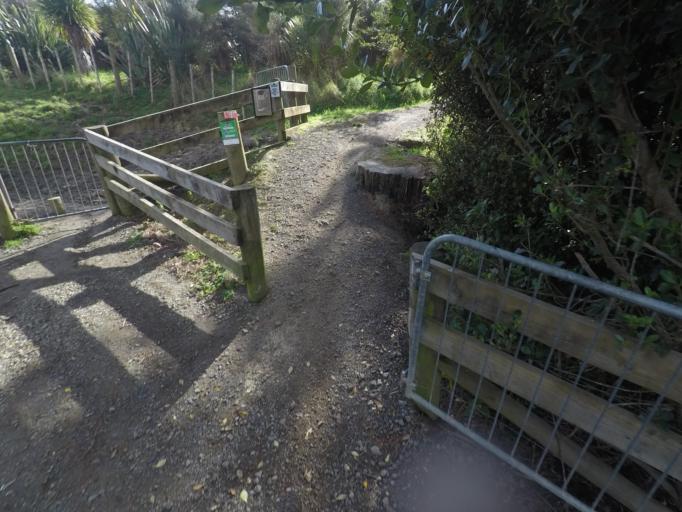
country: NZ
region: Auckland
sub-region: Auckland
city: Manukau City
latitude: -36.9993
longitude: 174.9107
